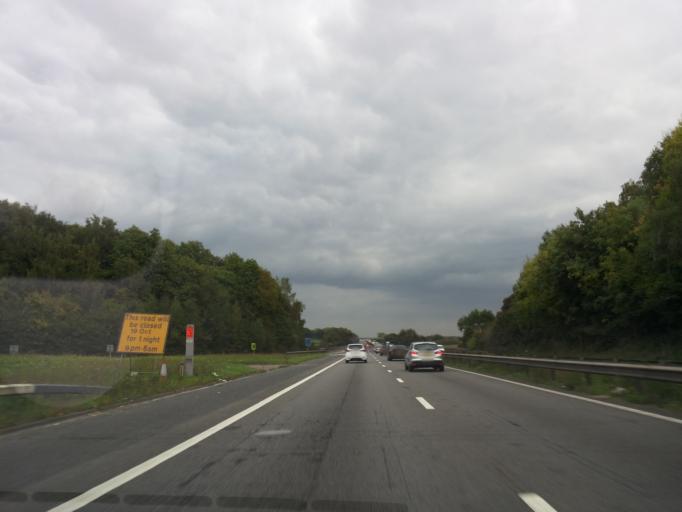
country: GB
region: England
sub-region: Kent
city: Newington
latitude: 51.3311
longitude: 0.6594
